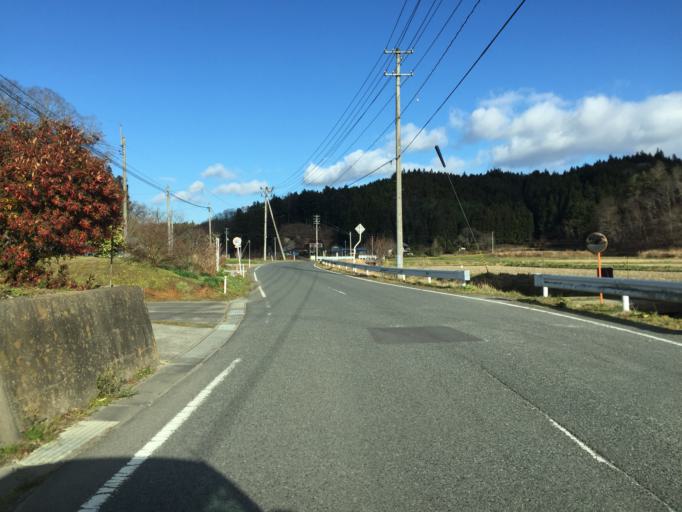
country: JP
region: Fukushima
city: Ishikawa
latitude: 37.2312
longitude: 140.6150
